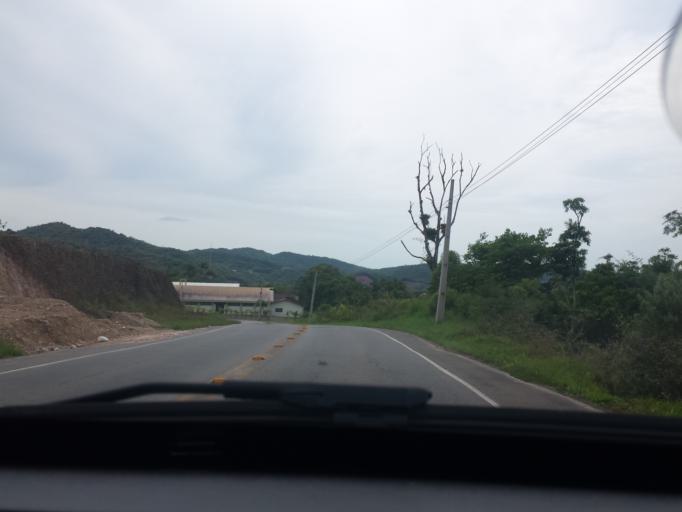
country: BR
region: Santa Catarina
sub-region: Blumenau
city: Blumenau
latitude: -26.8926
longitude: -49.0106
